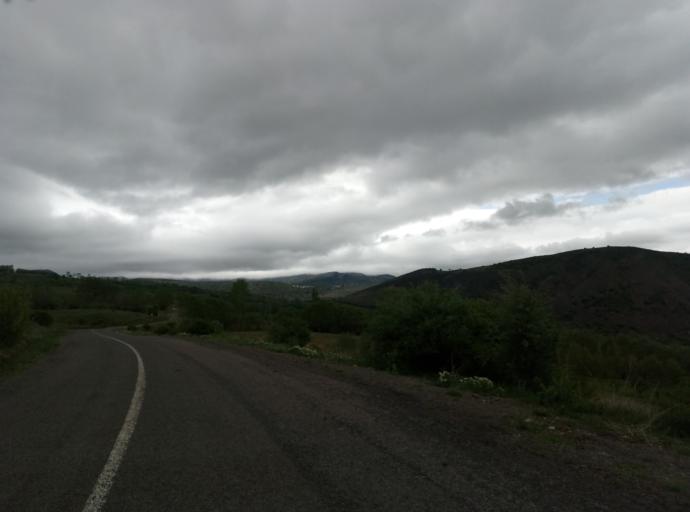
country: TR
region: Sivas
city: Aksu
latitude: 40.1838
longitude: 37.9337
